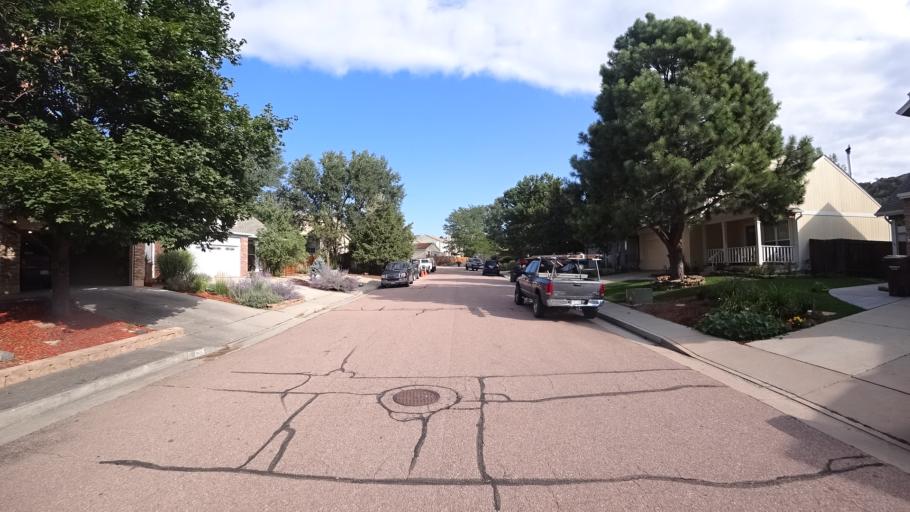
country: US
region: Colorado
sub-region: El Paso County
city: Air Force Academy
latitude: 38.9181
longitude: -104.8621
